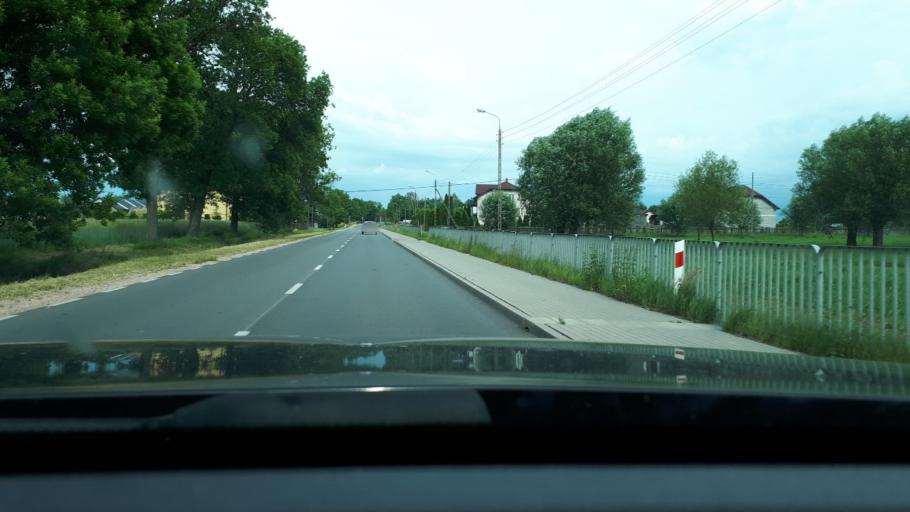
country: PL
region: Masovian Voivodeship
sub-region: Powiat warszawski zachodni
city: Kampinos
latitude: 52.2697
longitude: 20.4234
